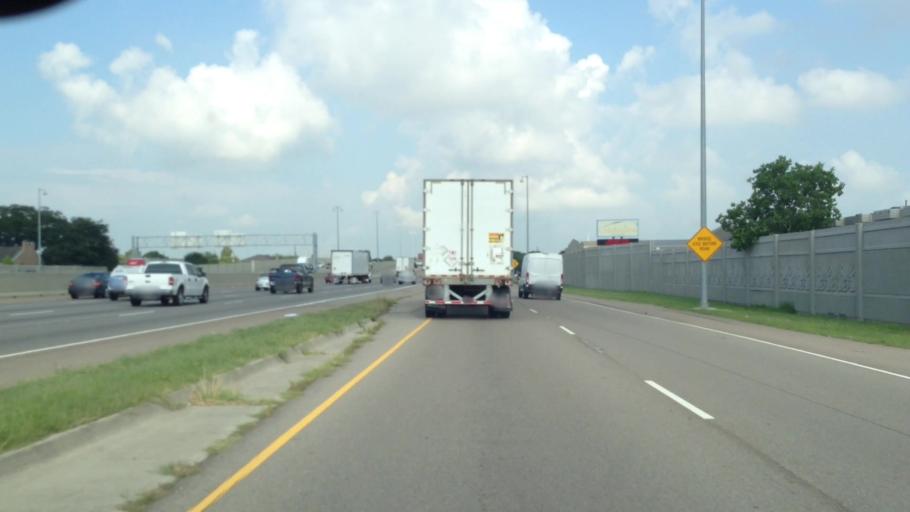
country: US
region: Louisiana
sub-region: Jefferson Parish
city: Metairie Terrace
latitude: 29.9998
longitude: -90.1888
